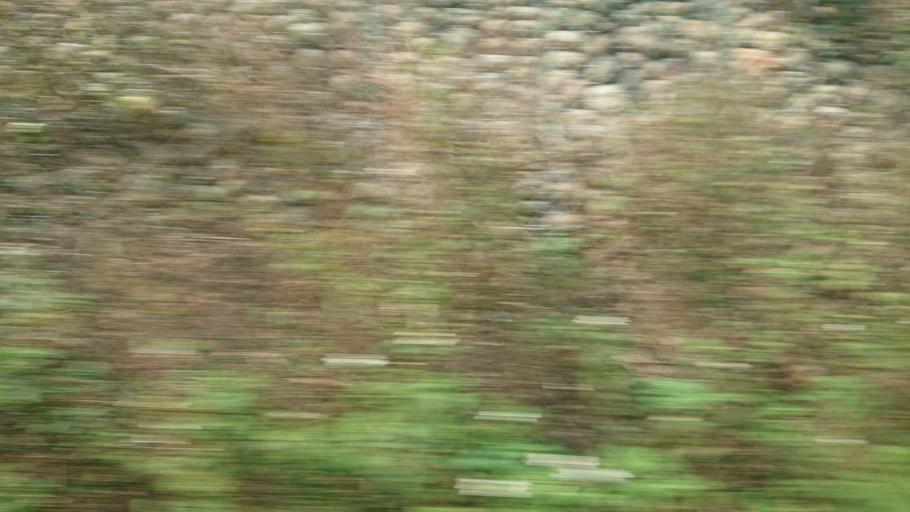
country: TW
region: Taiwan
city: Lugu
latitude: 23.7372
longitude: 120.6585
